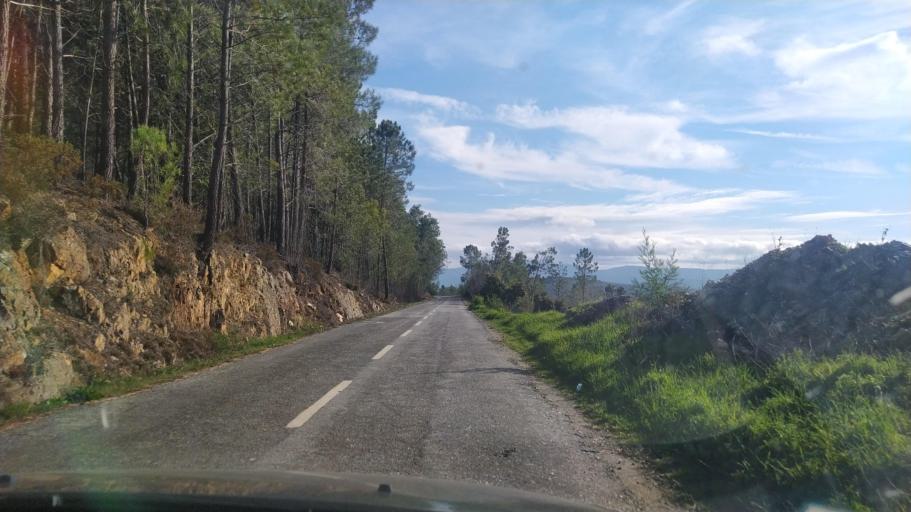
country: PT
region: Coimbra
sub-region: Oliveira do Hospital
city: Oliveira do Hospital
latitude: 40.1992
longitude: -7.7294
